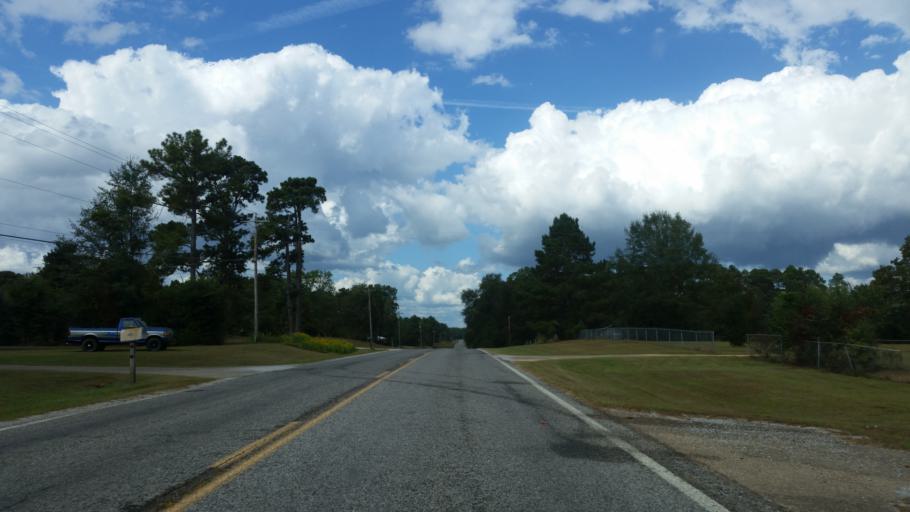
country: US
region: Mississippi
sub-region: Stone County
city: Wiggins
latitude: 30.8861
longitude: -89.1168
